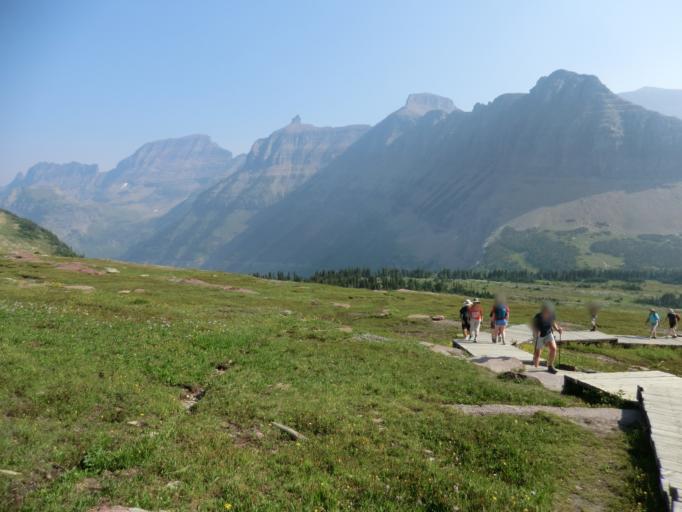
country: US
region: Montana
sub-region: Flathead County
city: Columbia Falls
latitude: 48.6940
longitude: -113.7259
